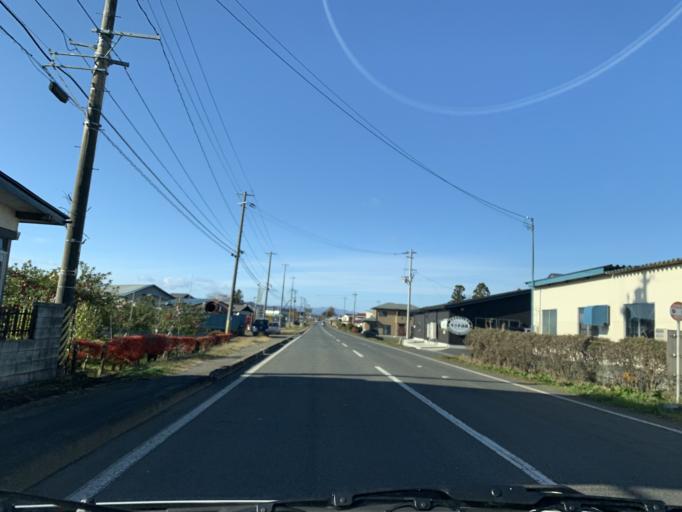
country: JP
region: Iwate
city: Mizusawa
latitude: 39.1750
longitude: 141.1391
